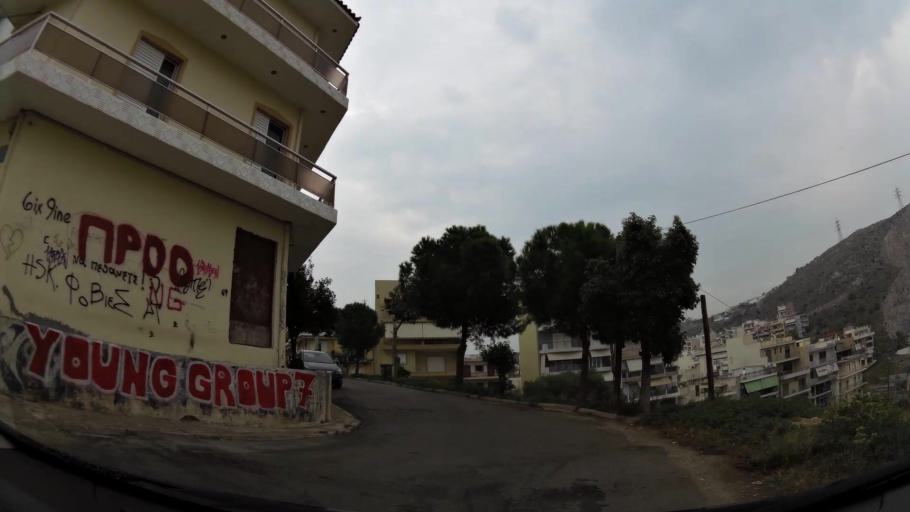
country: GR
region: Attica
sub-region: Nomos Piraios
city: Korydallos
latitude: 37.9938
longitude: 23.6413
